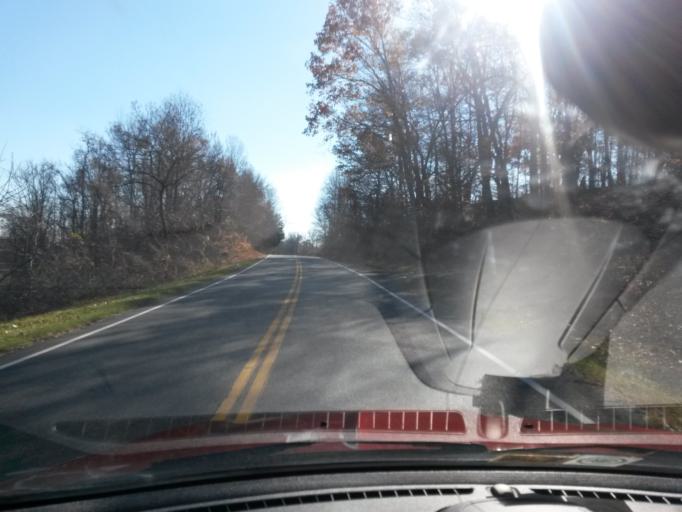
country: US
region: Virginia
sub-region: City of Bedford
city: Bedford
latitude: 37.4134
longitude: -79.5663
